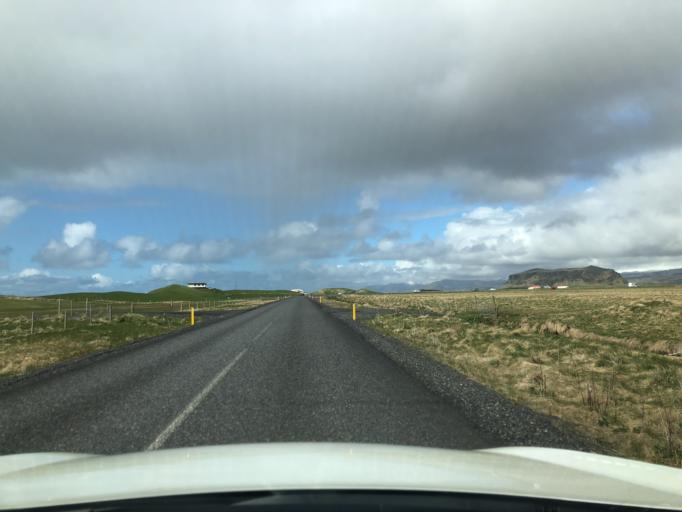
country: IS
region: South
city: Vestmannaeyjar
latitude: 63.4227
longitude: -19.1737
